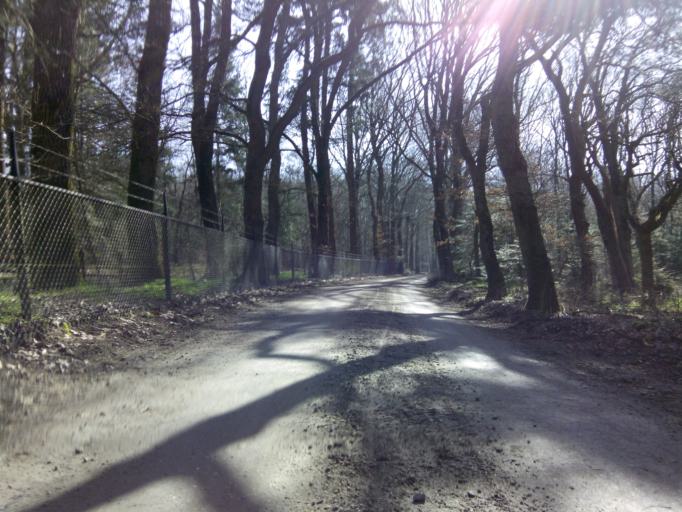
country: NL
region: Gelderland
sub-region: Gemeente Barneveld
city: Garderen
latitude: 52.2178
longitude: 5.7332
